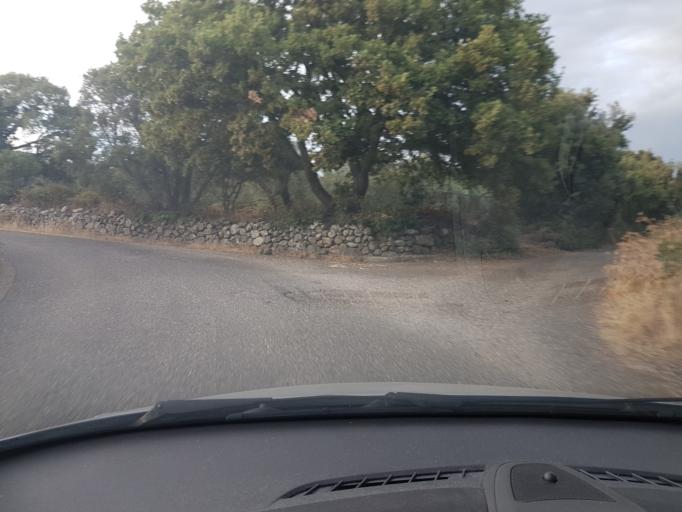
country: IT
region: Sardinia
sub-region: Provincia di Oristano
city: Seneghe
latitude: 40.0875
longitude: 8.6198
